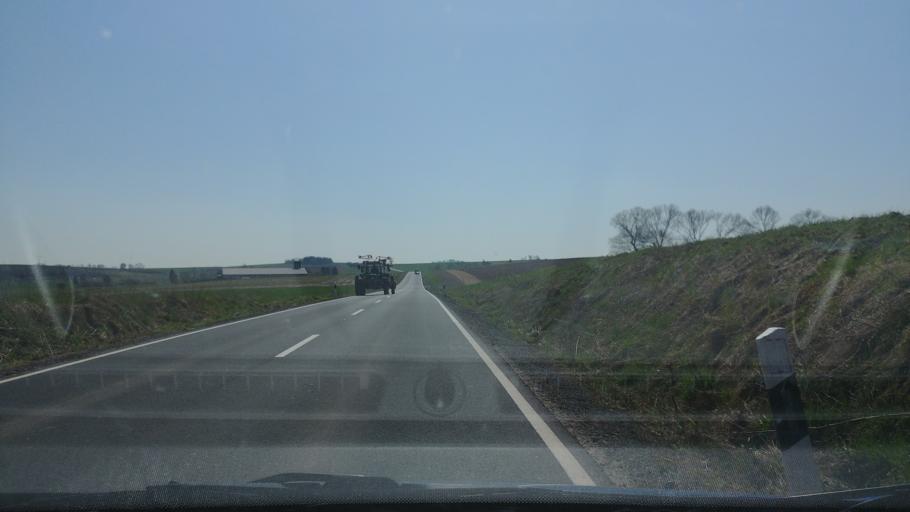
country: DE
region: Lower Saxony
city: Hillerse
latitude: 51.7309
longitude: 9.9379
